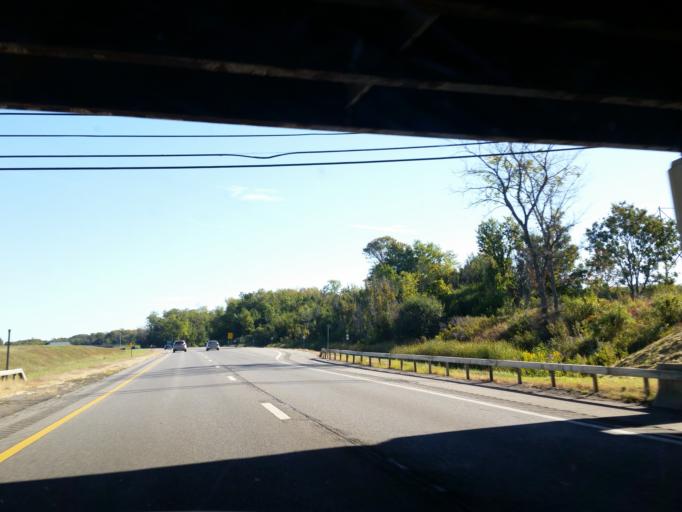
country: US
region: New York
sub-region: Erie County
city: Hamburg
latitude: 42.7405
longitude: -78.8465
